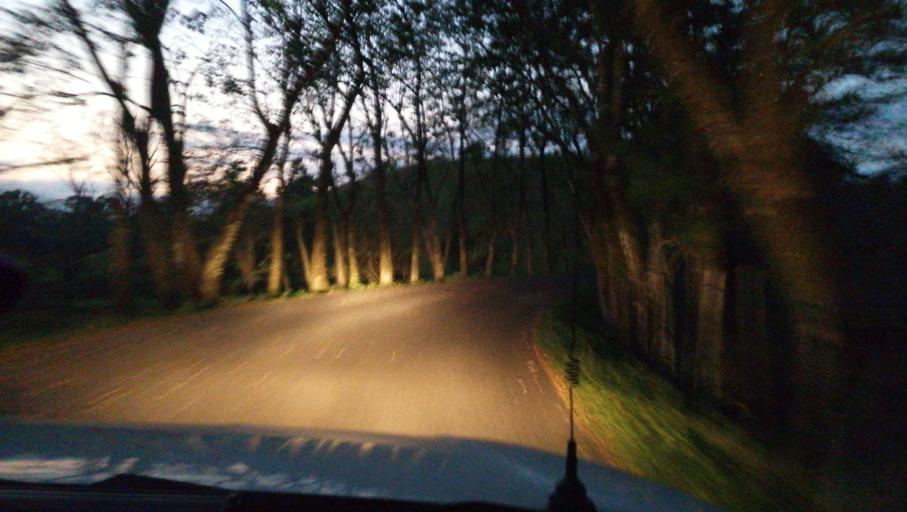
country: MX
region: Chiapas
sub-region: Ostuacan
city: Nuevo Juan del Grijalva
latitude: 17.4825
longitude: -93.3520
